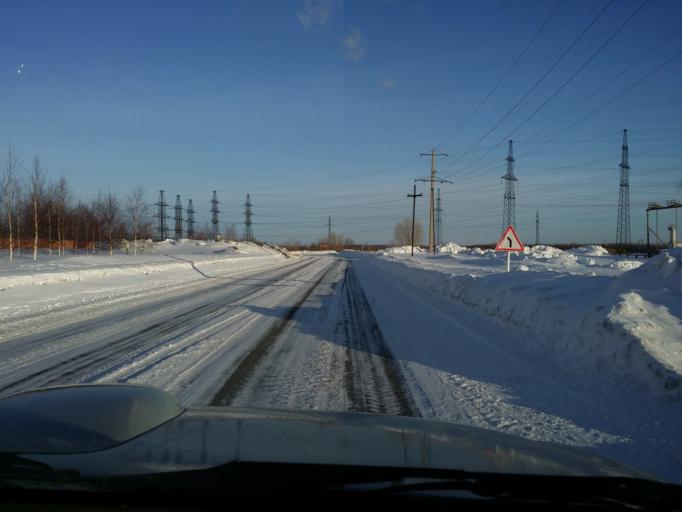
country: RU
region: Khanty-Mansiyskiy Avtonomnyy Okrug
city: Izluchinsk
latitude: 60.9732
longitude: 76.9415
